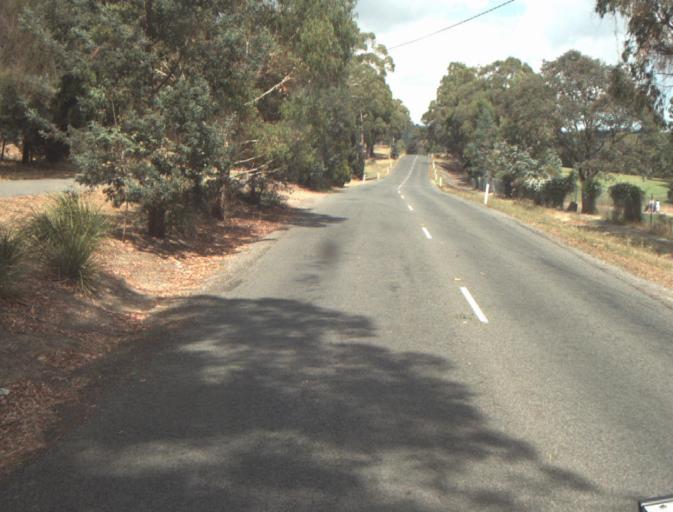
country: AU
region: Tasmania
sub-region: Launceston
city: Newstead
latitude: -41.4648
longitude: 147.1712
